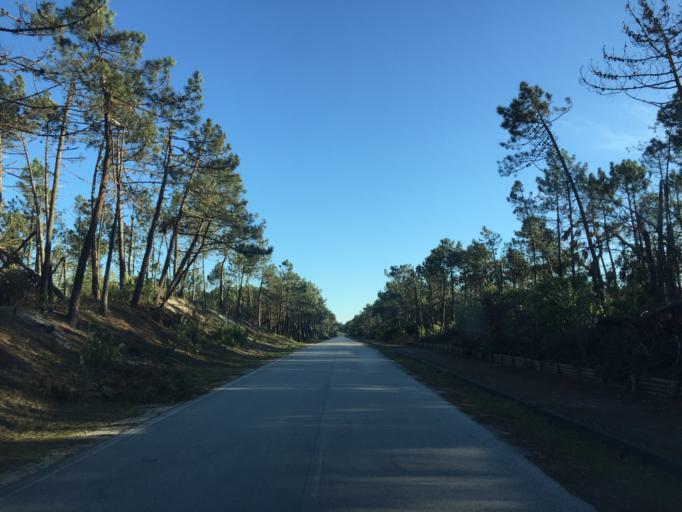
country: PT
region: Coimbra
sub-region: Figueira da Foz
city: Lavos
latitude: 40.0835
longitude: -8.8657
